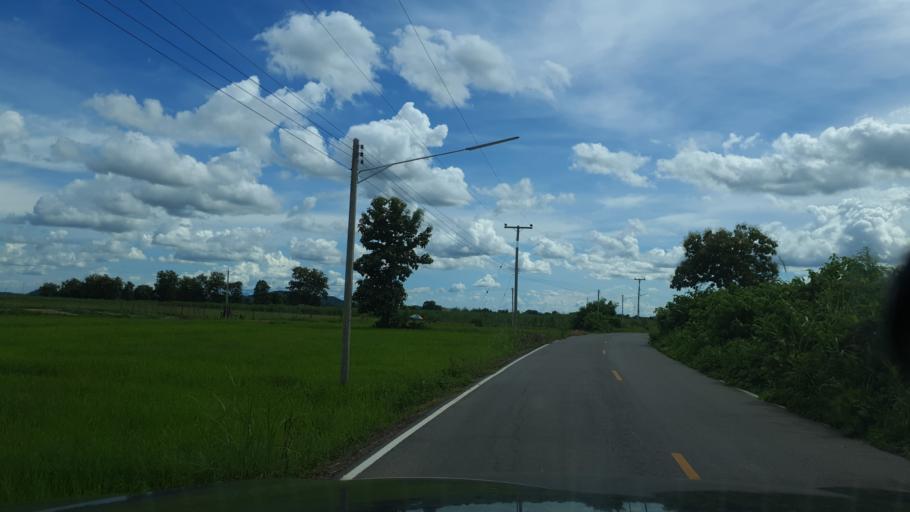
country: TH
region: Sukhothai
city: Thung Saliam
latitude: 17.3451
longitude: 99.6393
